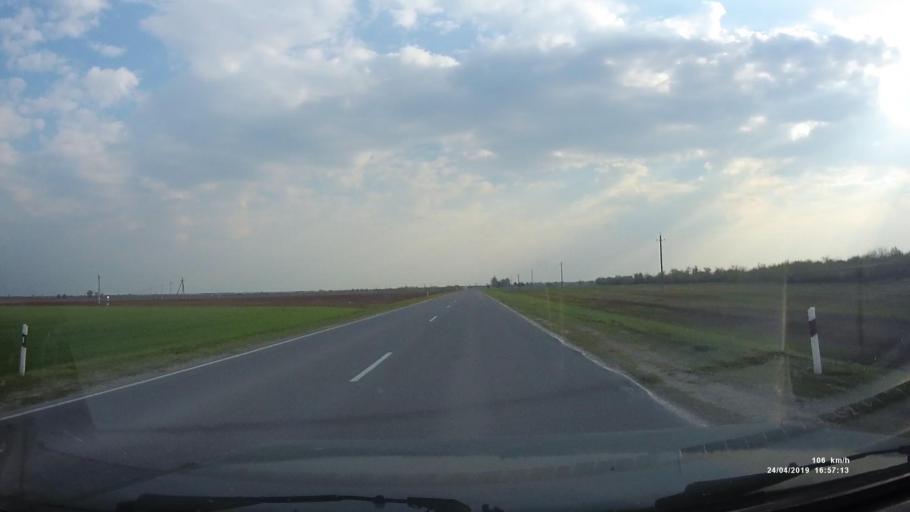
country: RU
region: Rostov
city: Proletarsk
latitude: 46.6399
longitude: 41.6705
